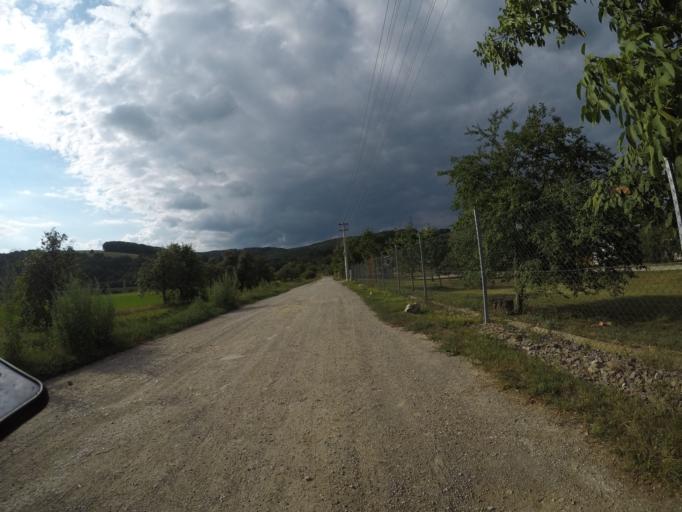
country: SK
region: Trenciansky
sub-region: Okres Trencin
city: Trencin
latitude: 48.9014
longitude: 17.9938
